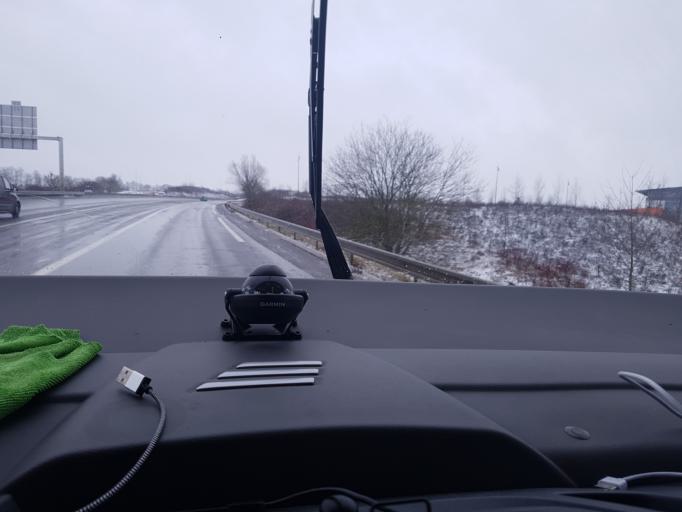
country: FR
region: Lorraine
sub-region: Departement de la Moselle
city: Peltre
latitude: 49.0927
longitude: 6.2307
